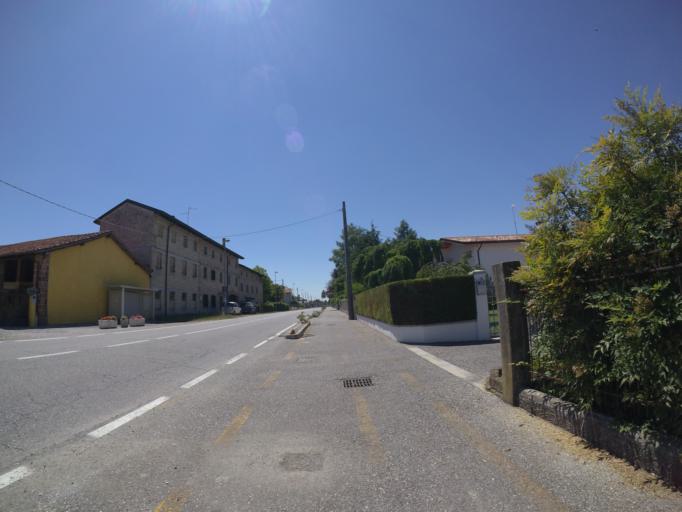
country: IT
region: Friuli Venezia Giulia
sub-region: Provincia di Udine
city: Teor
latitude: 45.8523
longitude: 13.0491
